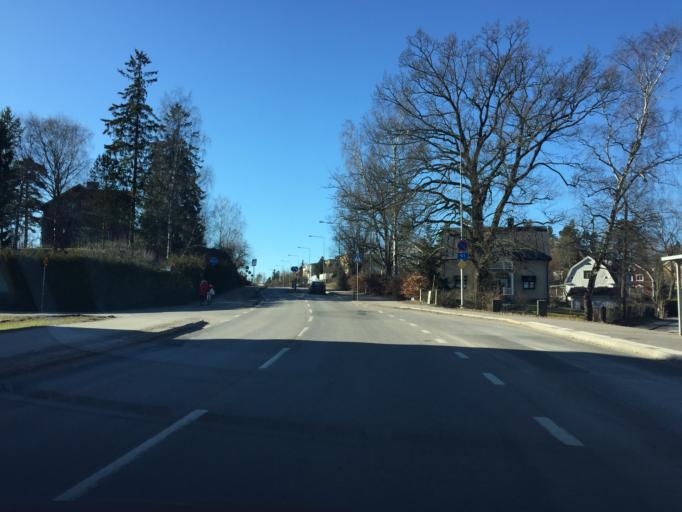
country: SE
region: OEstergoetland
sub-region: Finspangs Kommun
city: Finspang
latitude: 58.7092
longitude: 15.7596
